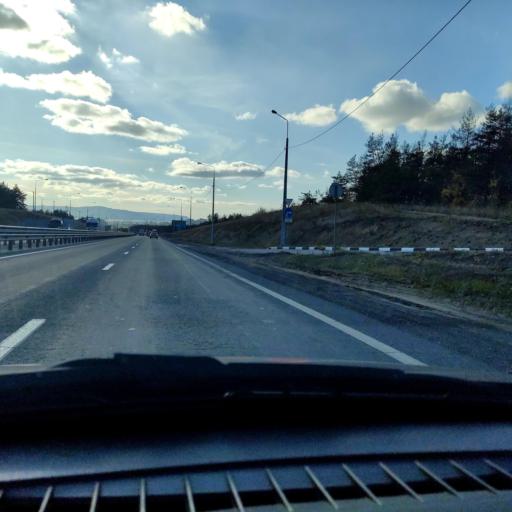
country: RU
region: Samara
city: Zhigulevsk
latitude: 53.4958
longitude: 49.5321
